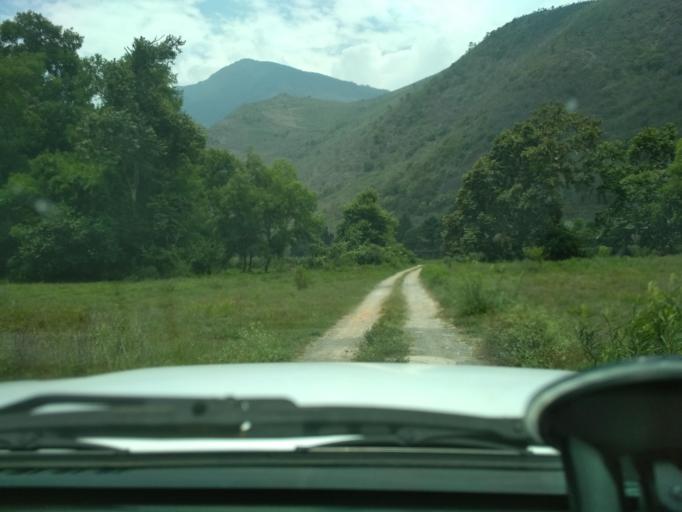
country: MX
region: Veracruz
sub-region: Nogales
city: Taza de Agua Ojo Zarco
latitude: 18.7768
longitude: -97.2081
